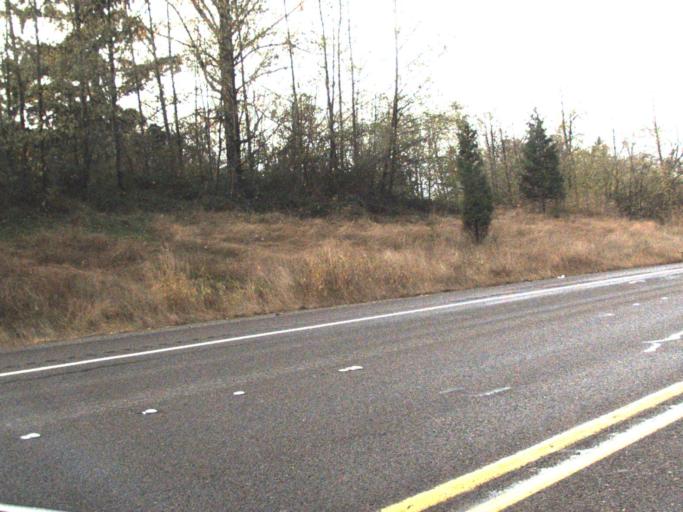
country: US
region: Washington
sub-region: Snohomish County
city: Fobes Hill
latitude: 47.9527
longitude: -122.1091
